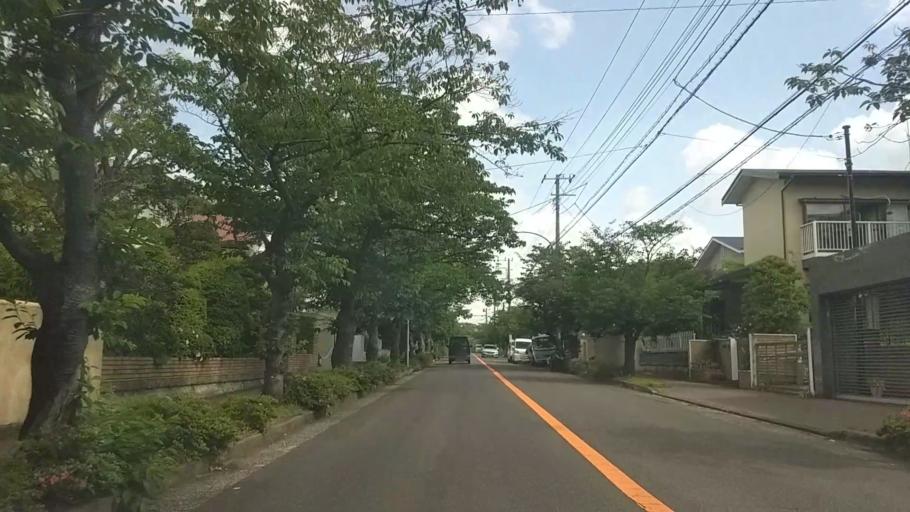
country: JP
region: Kanagawa
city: Zushi
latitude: 35.3124
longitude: 139.5769
